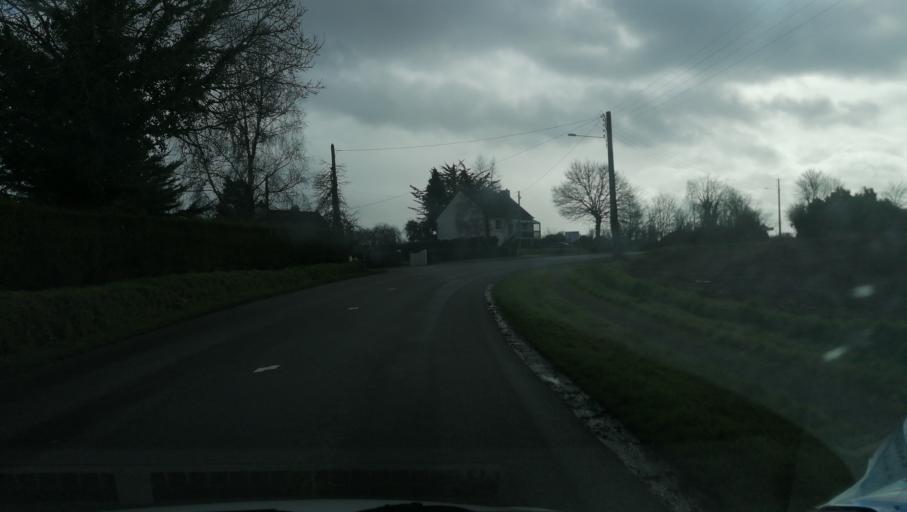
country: FR
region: Brittany
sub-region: Departement des Cotes-d'Armor
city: Plelo
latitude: 48.5811
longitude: -2.9174
